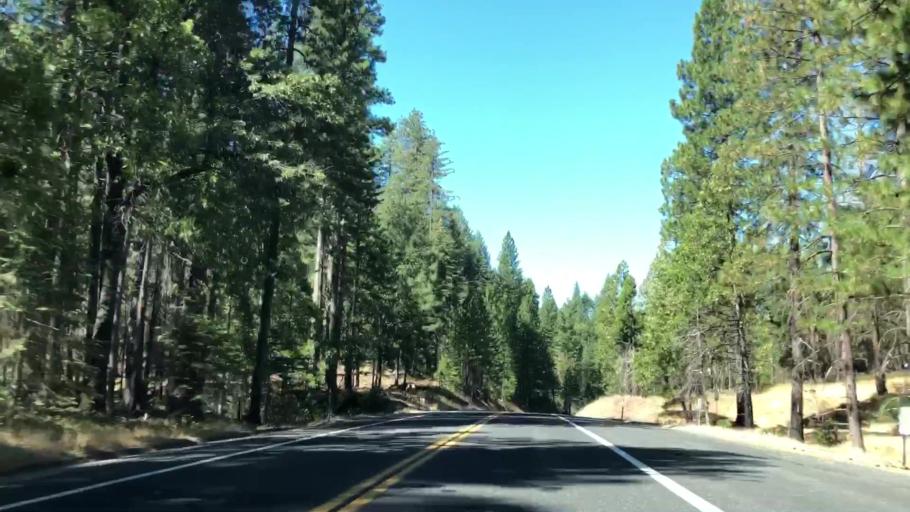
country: US
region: California
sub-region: Mariposa County
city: Midpines
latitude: 37.8134
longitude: -119.8922
